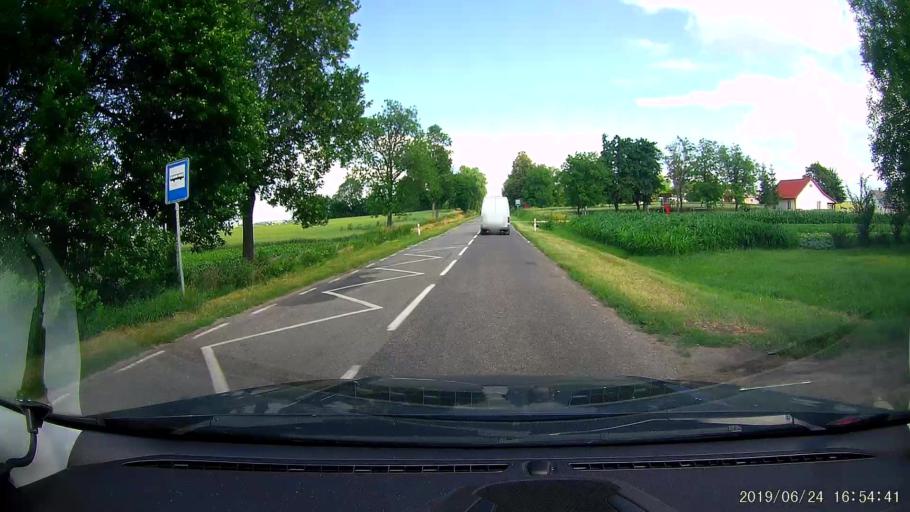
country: PL
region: Lublin Voivodeship
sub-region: Powiat tomaszowski
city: Telatyn
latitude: 50.5309
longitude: 23.8184
